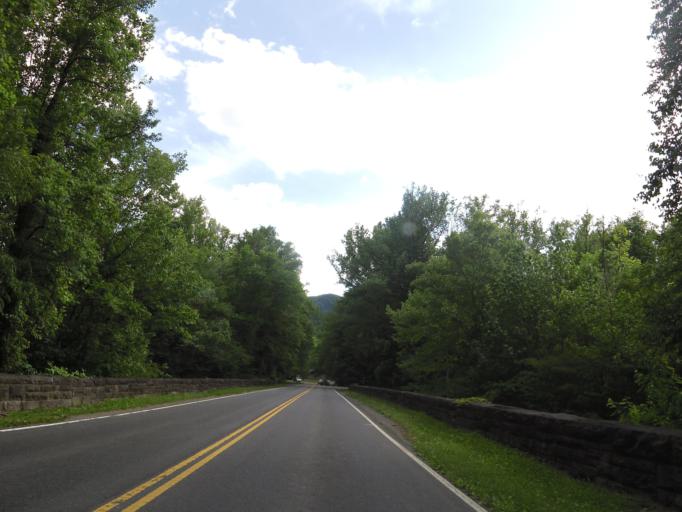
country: US
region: Tennessee
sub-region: Sevier County
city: Gatlinburg
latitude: 35.6881
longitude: -83.5351
